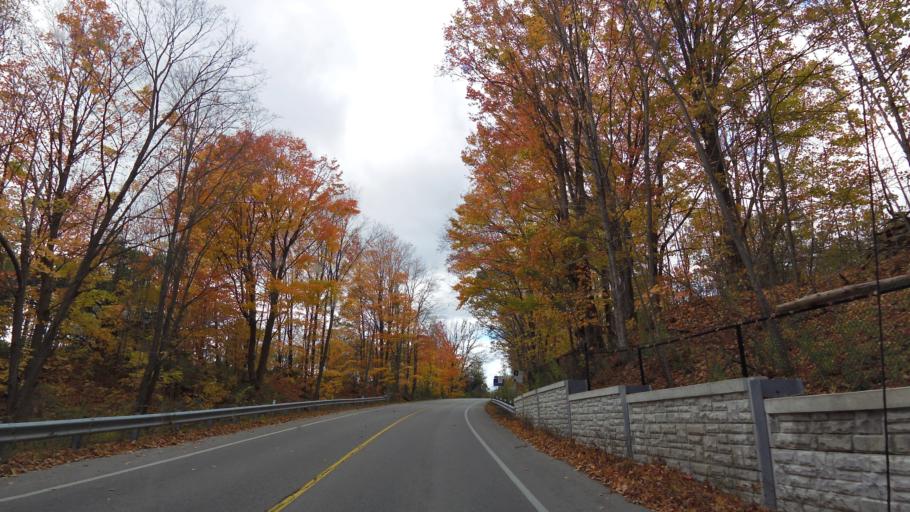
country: CA
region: Ontario
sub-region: Halton
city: Milton
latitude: 43.4991
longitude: -79.7790
